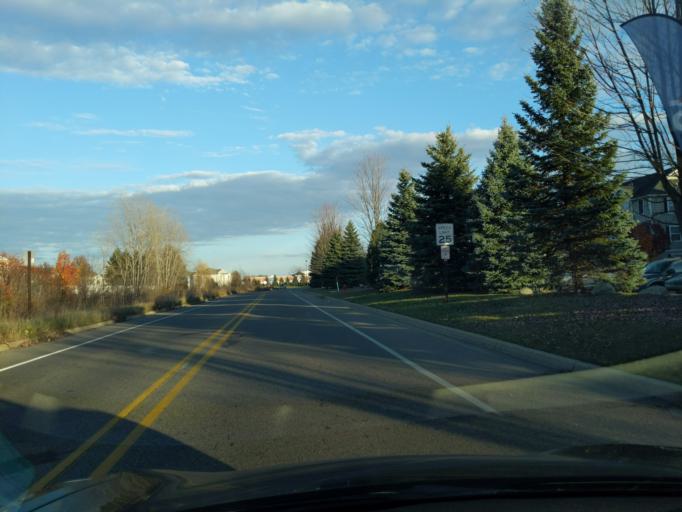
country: US
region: Michigan
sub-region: Ingham County
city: East Lansing
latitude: 42.7730
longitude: -84.4905
